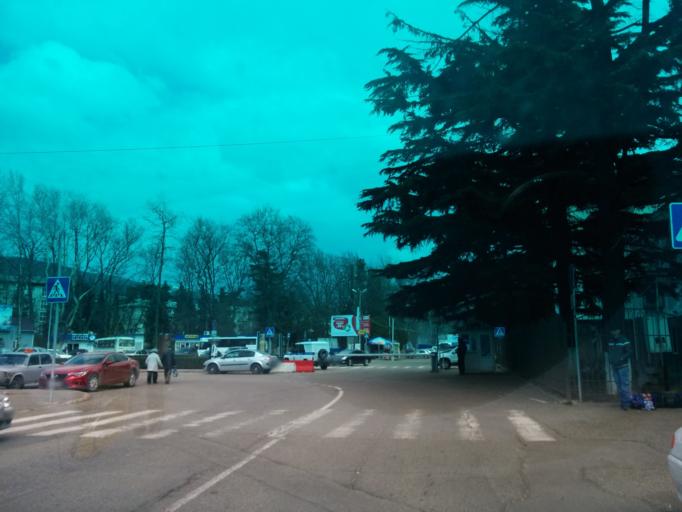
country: RU
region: Krasnodarskiy
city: Tuapse
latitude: 44.0971
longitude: 39.0827
